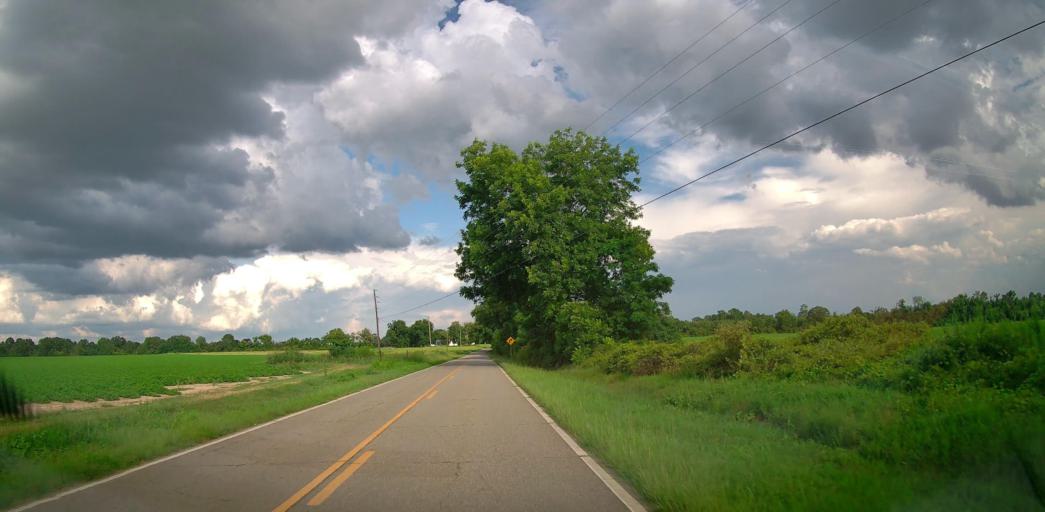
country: US
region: Georgia
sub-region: Bleckley County
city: Cochran
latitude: 32.4074
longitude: -83.3846
